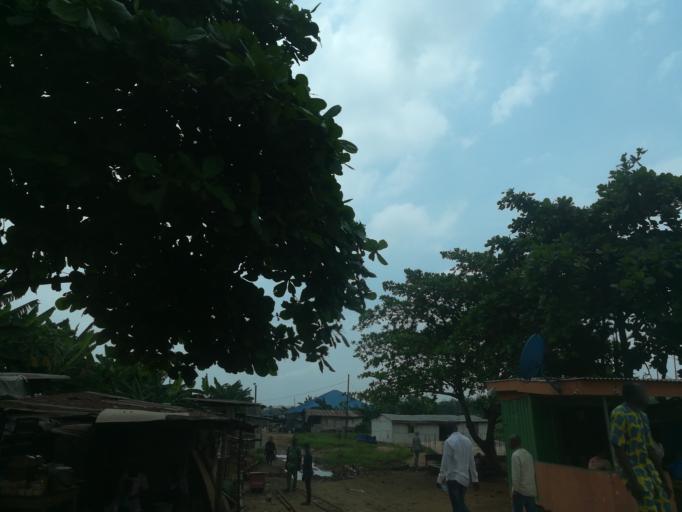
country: NG
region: Lagos
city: Ikorodu
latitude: 6.6163
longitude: 3.5139
